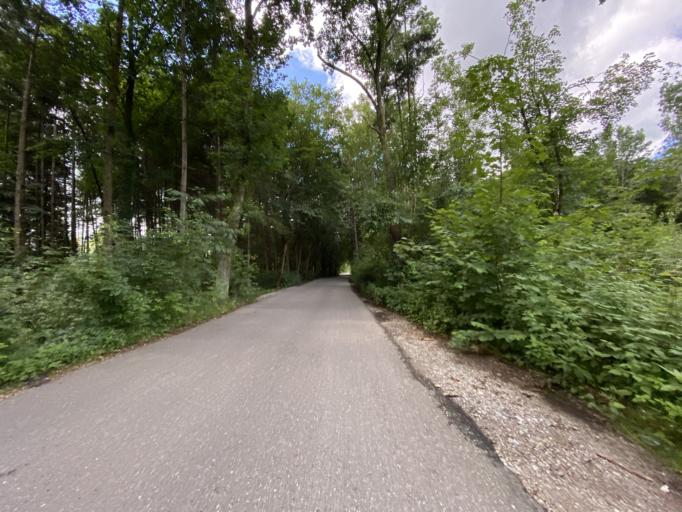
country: DE
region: Bavaria
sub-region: Upper Bavaria
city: Gilching
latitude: 48.0979
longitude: 11.3028
